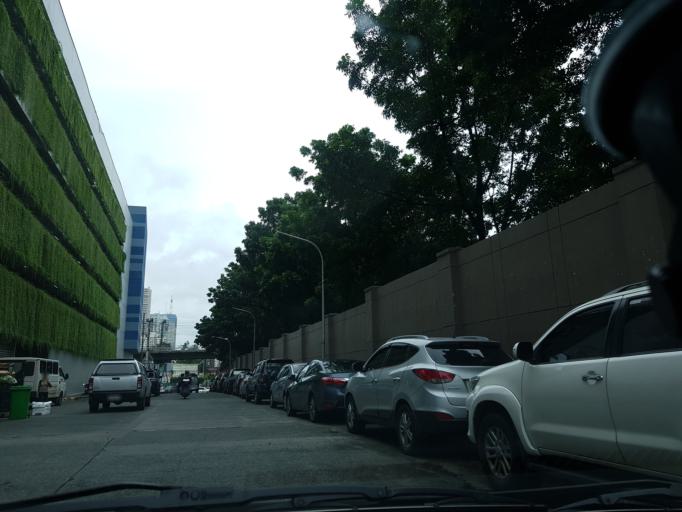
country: PH
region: Metro Manila
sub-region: Pasig
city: Pasig City
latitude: 14.5869
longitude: 121.0577
